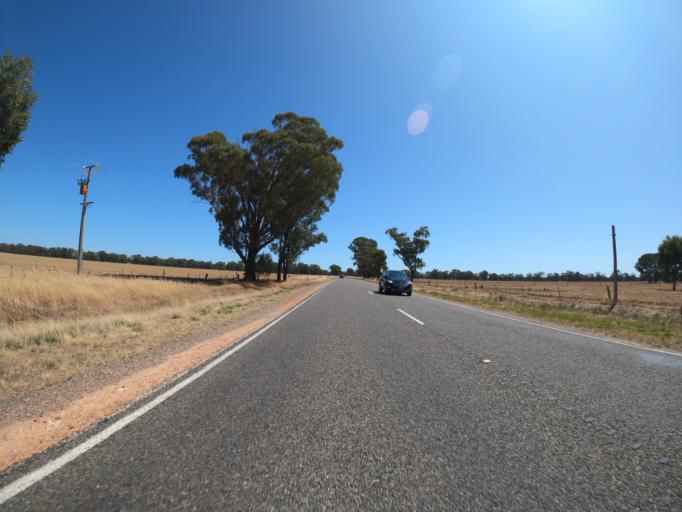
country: AU
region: New South Wales
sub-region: Corowa Shire
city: Corowa
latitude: -36.0780
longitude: 146.3433
